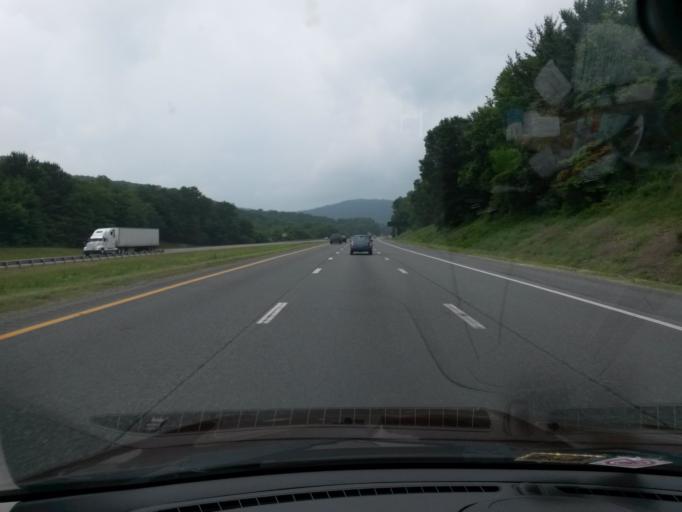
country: US
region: Virginia
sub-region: City of Waynesboro
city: Waynesboro
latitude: 38.0466
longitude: -78.9054
